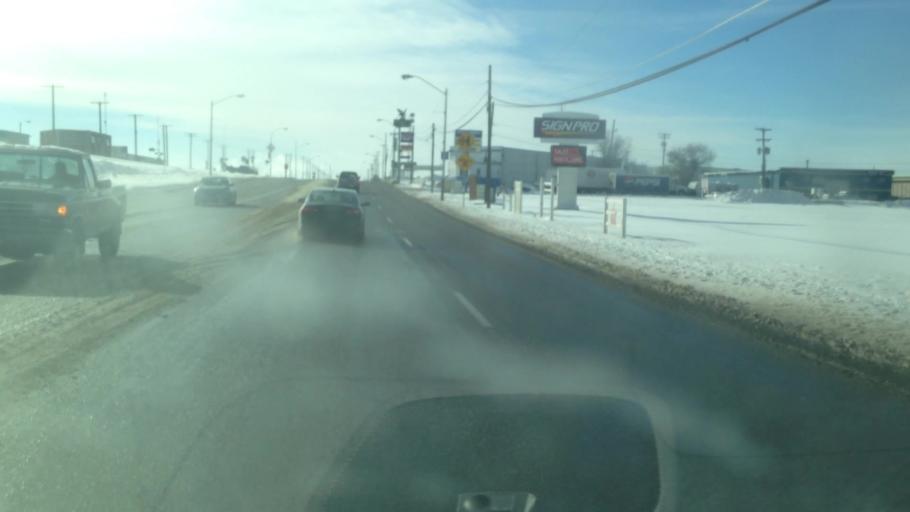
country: US
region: Idaho
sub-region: Bonneville County
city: Idaho Falls
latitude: 43.4827
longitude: -112.0454
